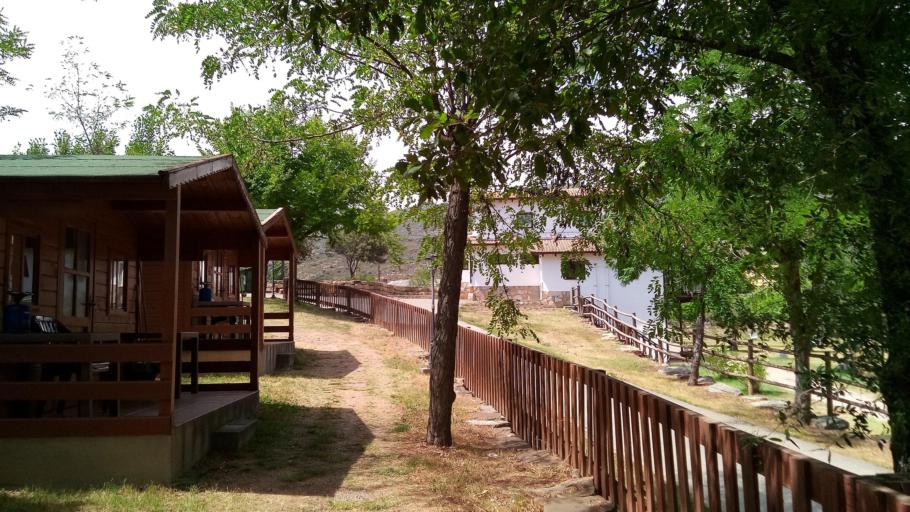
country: ES
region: Aragon
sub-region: Provincia de Huesca
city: Castigaleu
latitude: 42.3087
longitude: 0.5458
